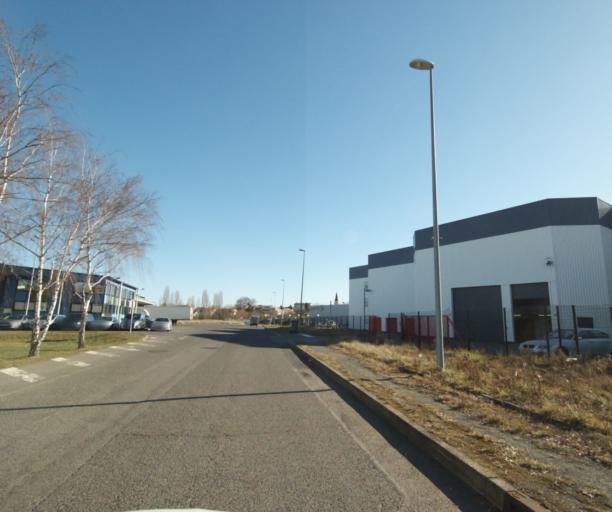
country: FR
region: Lorraine
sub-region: Departement de Meurthe-et-Moselle
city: Vandoeuvre-les-Nancy
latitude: 48.6565
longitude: 6.1914
